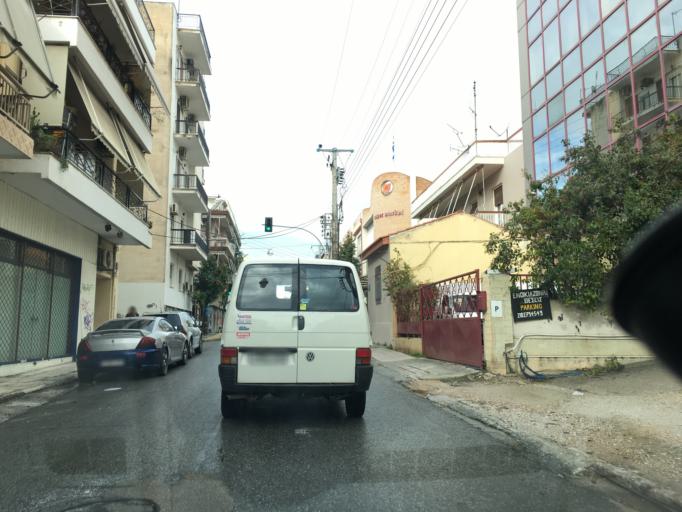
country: GR
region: Attica
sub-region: Nomarchia Athinas
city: Nea Ionia
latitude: 38.0375
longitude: 23.7720
